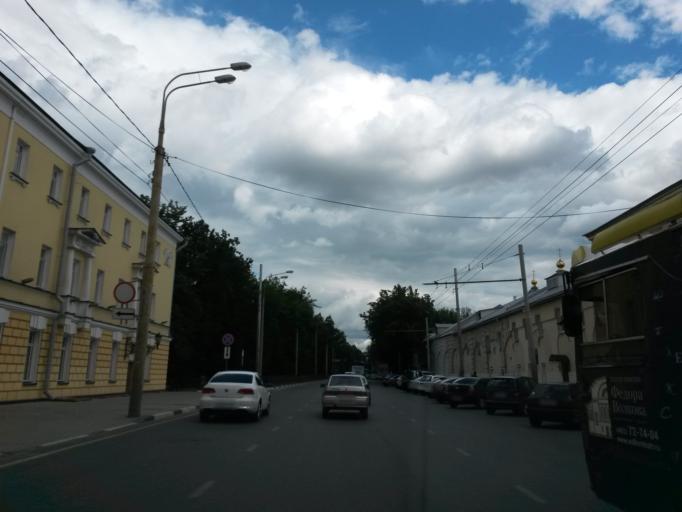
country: RU
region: Jaroslavl
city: Yaroslavl
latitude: 57.6271
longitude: 39.8853
